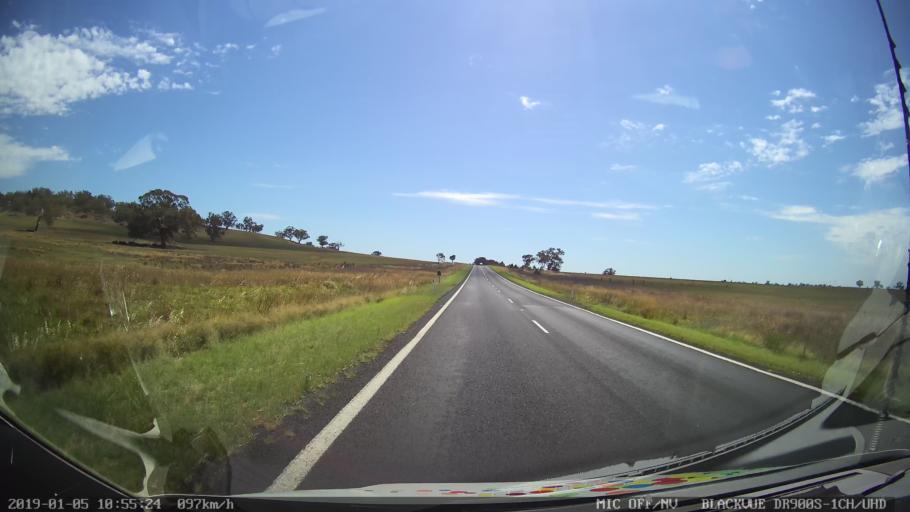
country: AU
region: New South Wales
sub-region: Warrumbungle Shire
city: Coonabarabran
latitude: -31.4485
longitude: 149.1433
